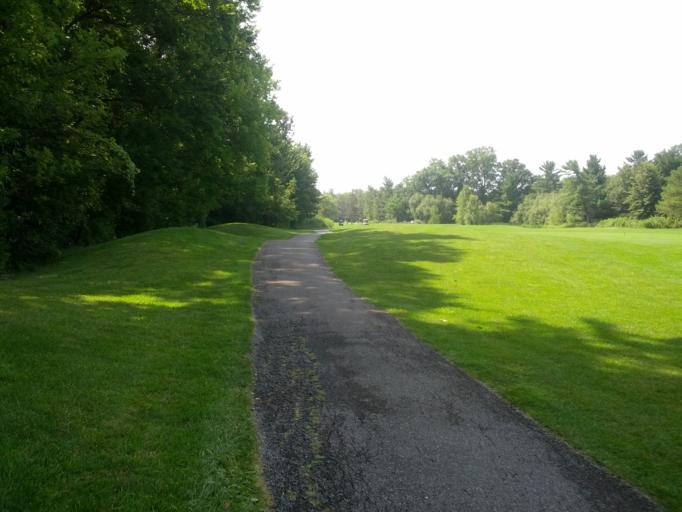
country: US
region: Ohio
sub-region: Cuyahoga County
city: Olmsted Falls
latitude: 41.3968
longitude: -81.9080
